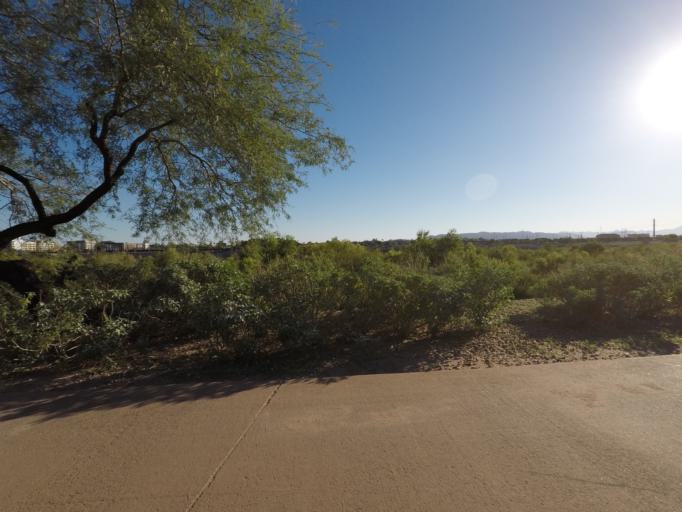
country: US
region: Arizona
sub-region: Maricopa County
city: Tempe Junction
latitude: 33.4355
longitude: -111.9522
